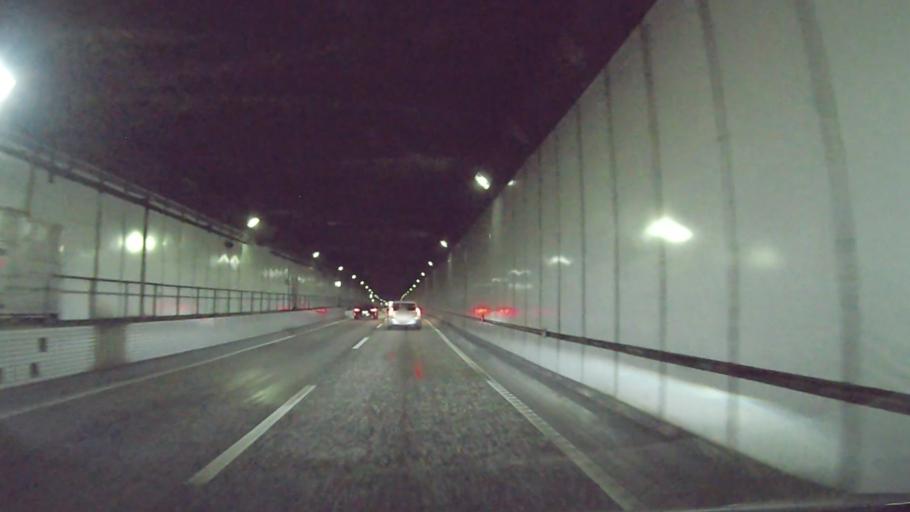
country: JP
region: Tokyo
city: Musashino
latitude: 35.7269
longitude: 139.6144
